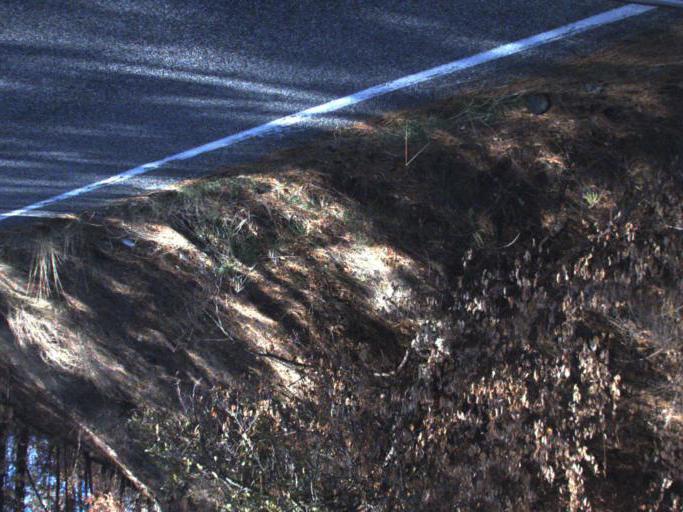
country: US
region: Washington
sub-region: Okanogan County
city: Coulee Dam
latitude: 48.0477
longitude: -118.6701
